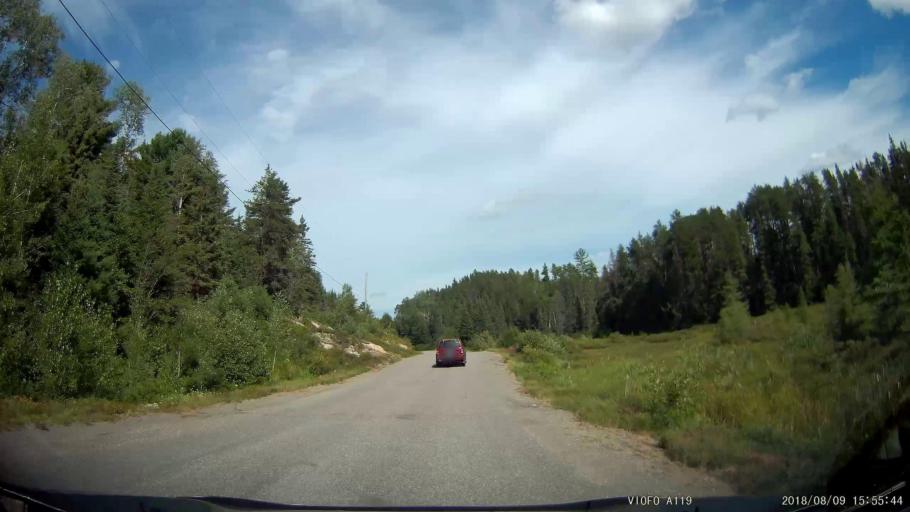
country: CA
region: Ontario
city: Rayside-Balfour
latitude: 46.6044
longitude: -81.5214
